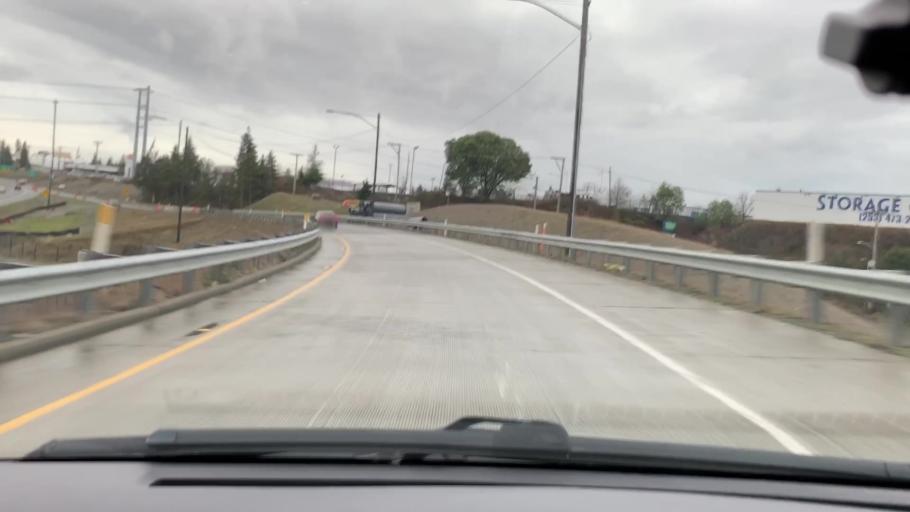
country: US
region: Washington
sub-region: Pierce County
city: Tacoma
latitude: 47.2304
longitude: -122.4634
